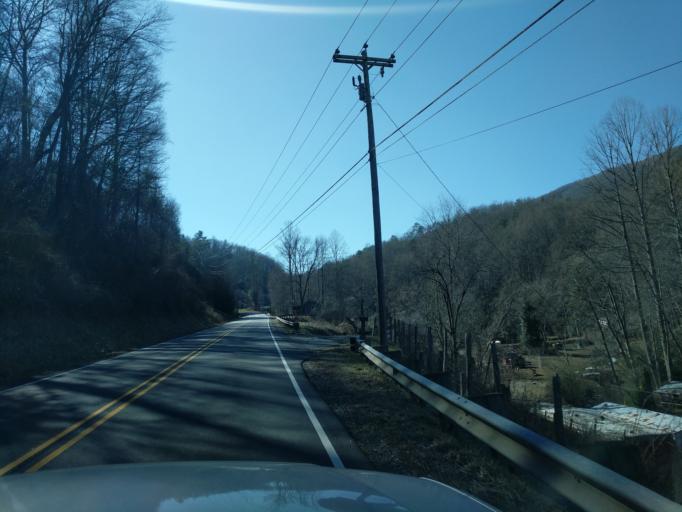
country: US
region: North Carolina
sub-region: Graham County
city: Robbinsville
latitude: 35.2558
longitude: -83.6944
